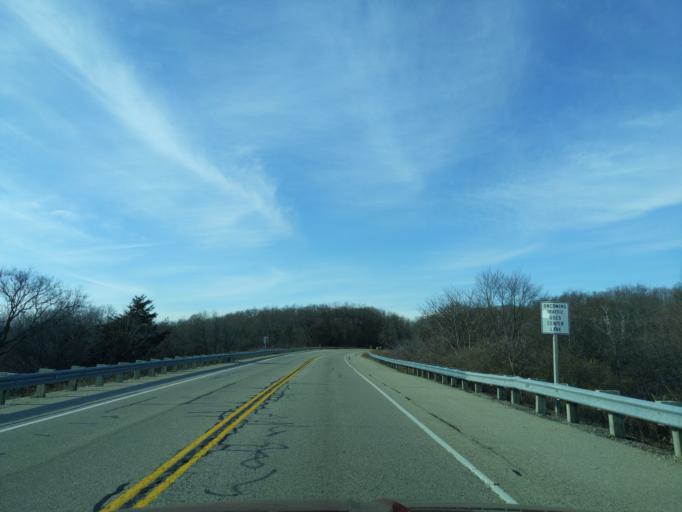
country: US
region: Wisconsin
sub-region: Walworth County
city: Whitewater
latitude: 42.7988
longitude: -88.6435
